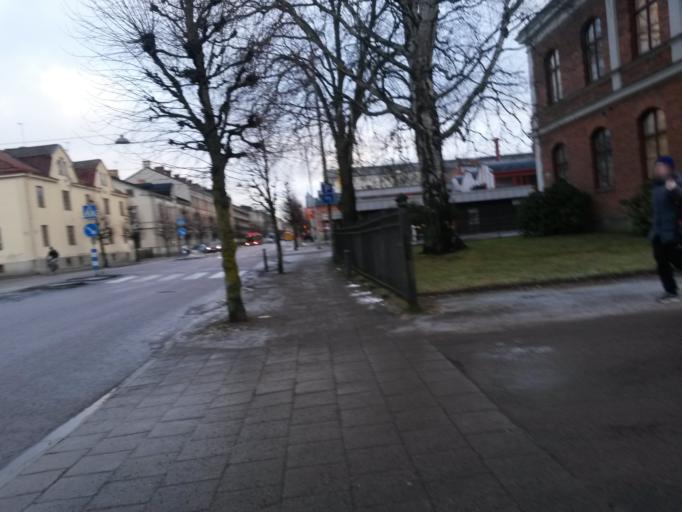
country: SE
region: Vaermland
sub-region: Karlstads Kommun
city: Karlstad
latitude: 59.3793
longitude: 13.4918
